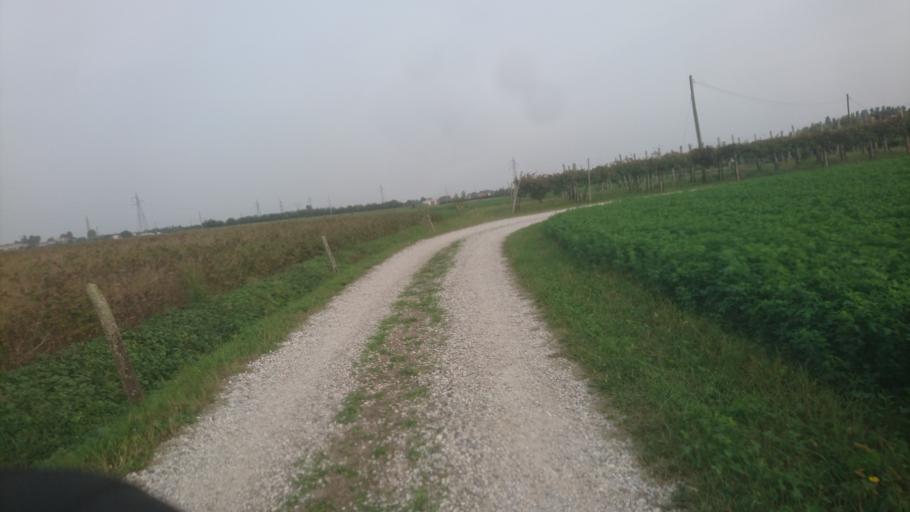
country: IT
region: Veneto
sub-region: Provincia di Vicenza
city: Montegalda
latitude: 45.4367
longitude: 11.6830
